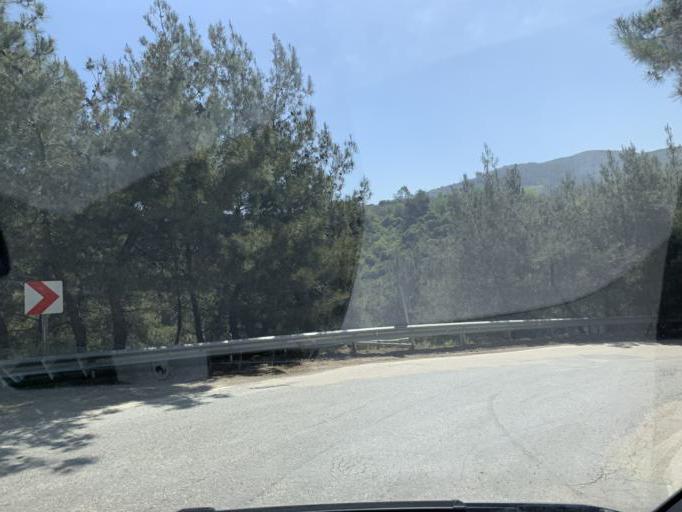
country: TR
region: Bursa
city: Niluefer
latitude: 40.3561
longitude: 28.9582
